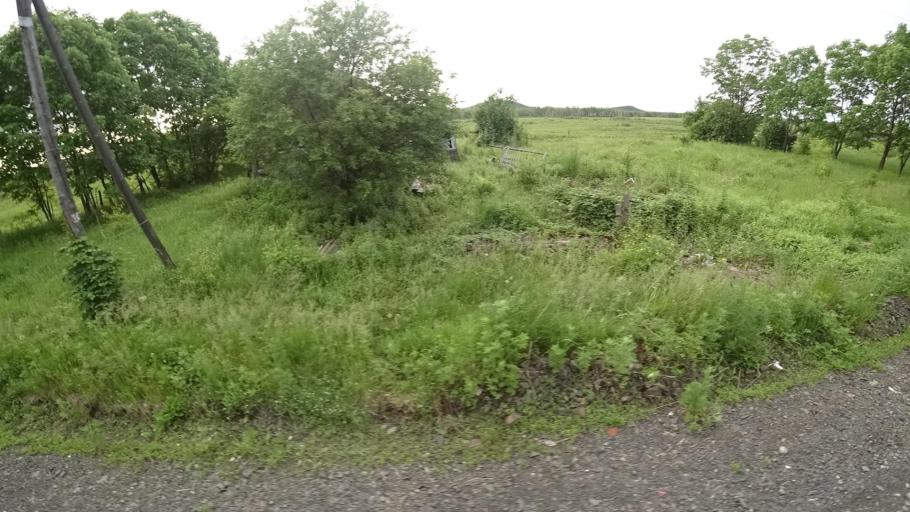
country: RU
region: Khabarovsk Krai
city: Amursk
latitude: 49.8891
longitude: 136.1293
